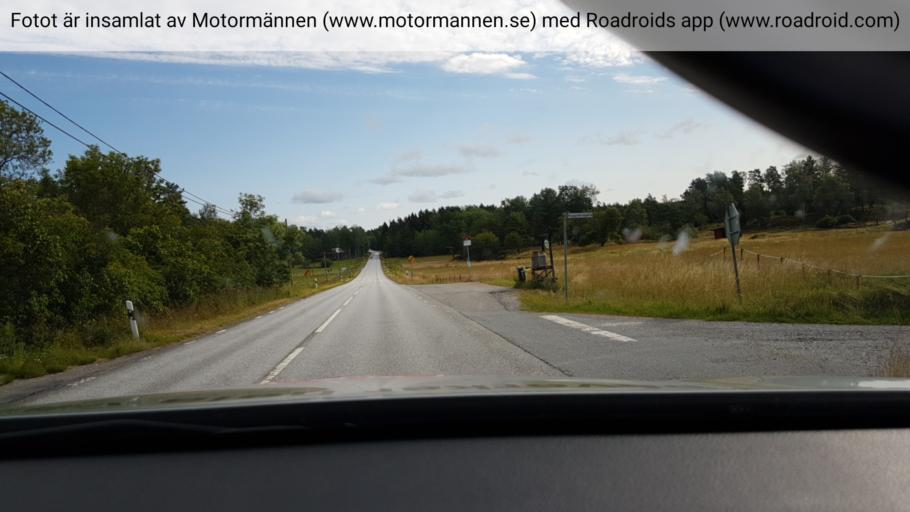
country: SE
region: Stockholm
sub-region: Vaxholms Kommun
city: Resaro
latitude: 59.5433
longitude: 18.4752
